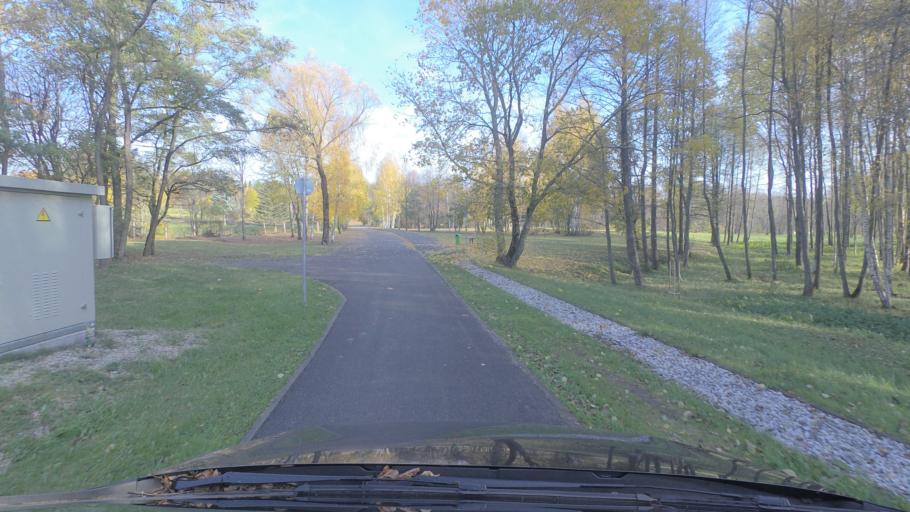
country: LT
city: Ignalina
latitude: 55.3363
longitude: 26.1475
